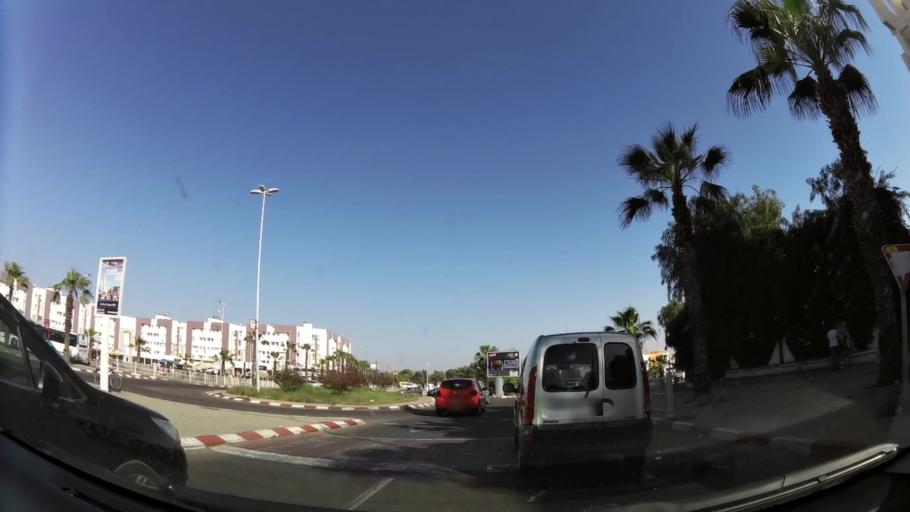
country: MA
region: Oued ed Dahab-Lagouira
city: Dakhla
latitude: 30.4057
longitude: -9.5517
